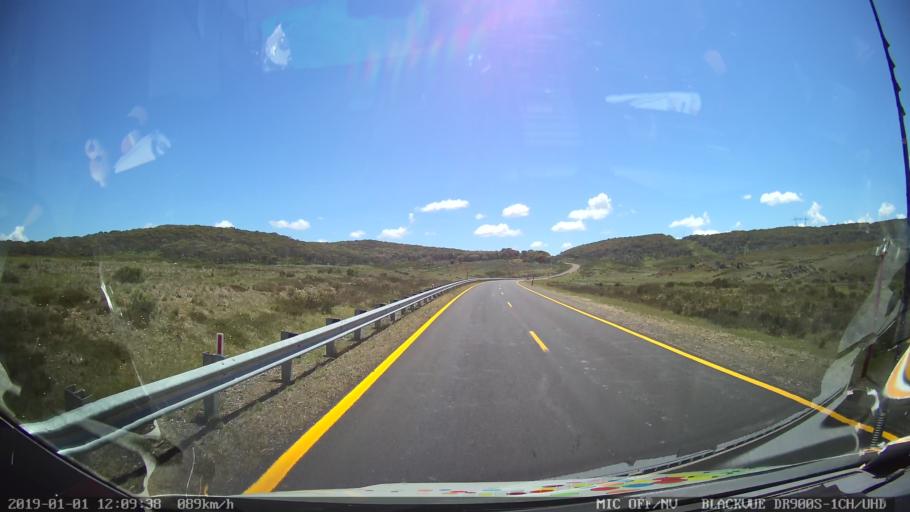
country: AU
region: New South Wales
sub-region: Tumut Shire
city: Tumut
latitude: -35.8051
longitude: 148.4963
